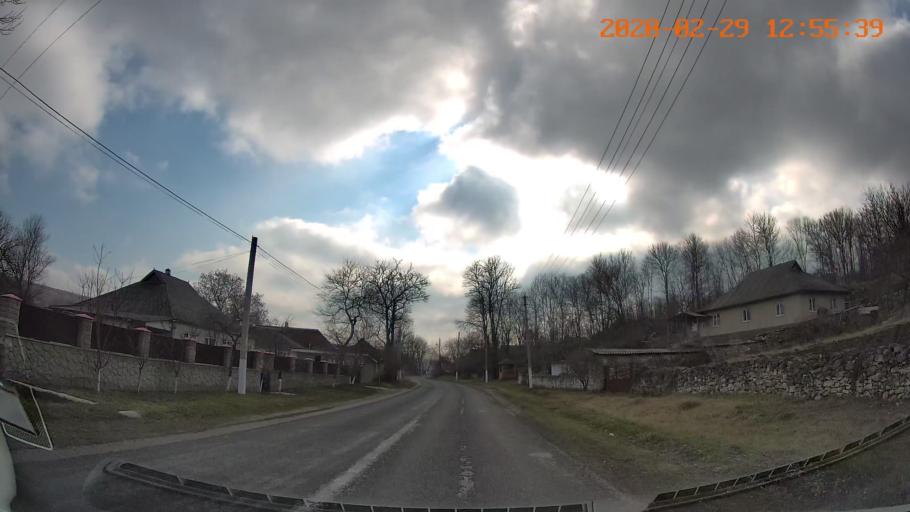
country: MD
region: Telenesti
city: Camenca
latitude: 48.0930
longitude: 28.7241
